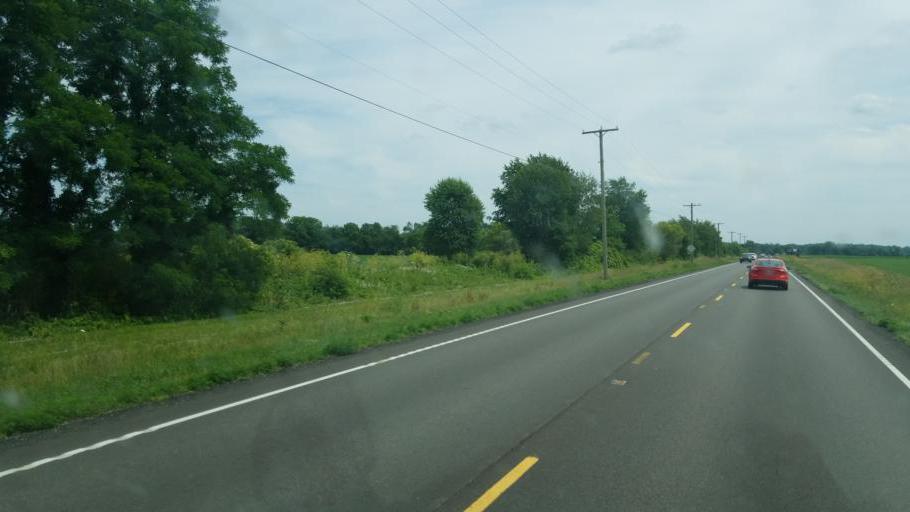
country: US
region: Ohio
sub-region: Knox County
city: Fredericktown
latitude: 40.4395
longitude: -82.5223
